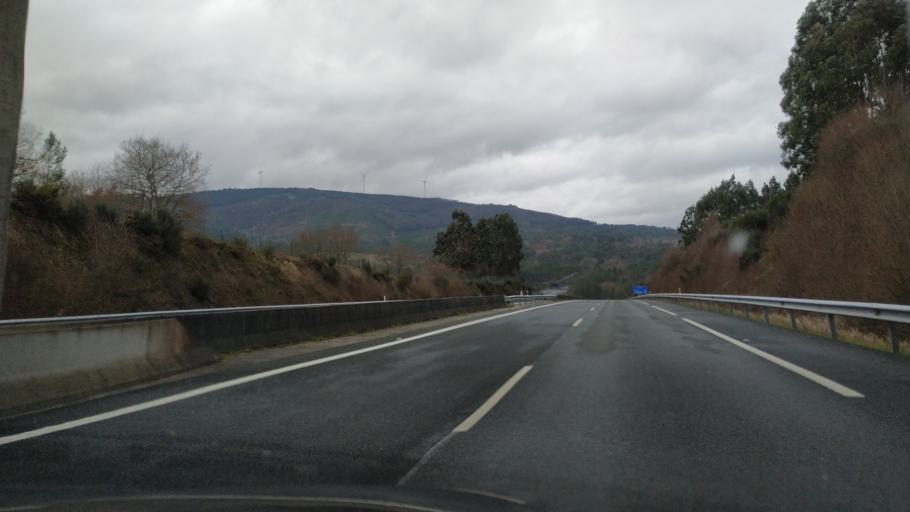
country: ES
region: Galicia
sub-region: Provincia de Ourense
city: Pinor
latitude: 42.4905
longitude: -8.0240
